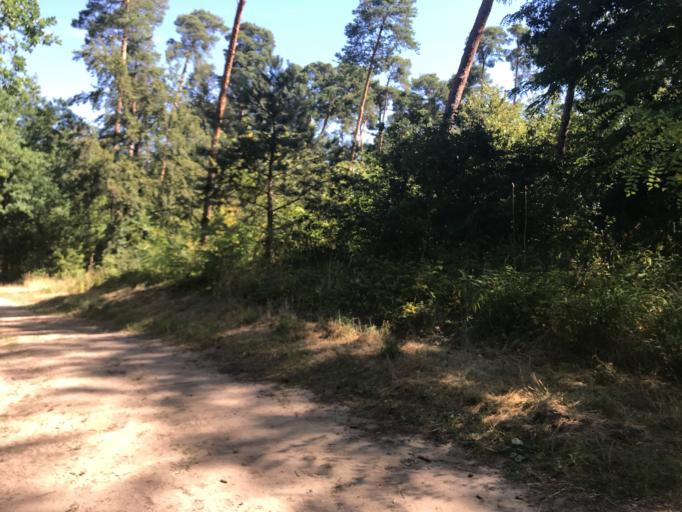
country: DE
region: Rheinland-Pfalz
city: Budenheim
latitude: 50.0151
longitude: 8.1599
